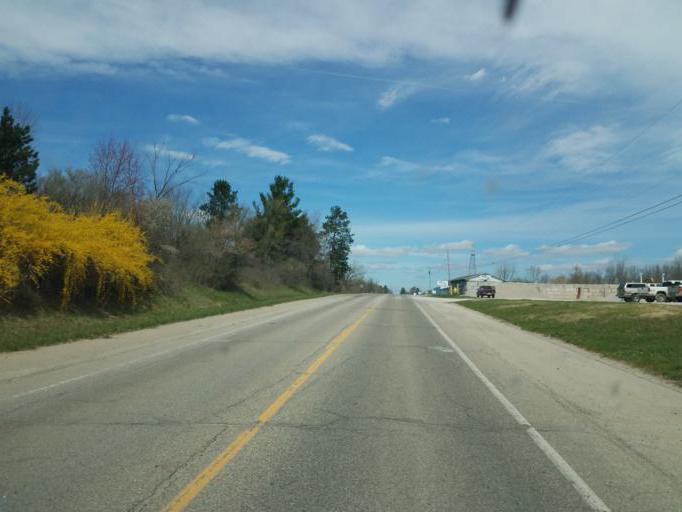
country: US
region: Michigan
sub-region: Isabella County
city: Mount Pleasant
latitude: 43.6308
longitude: -84.7680
